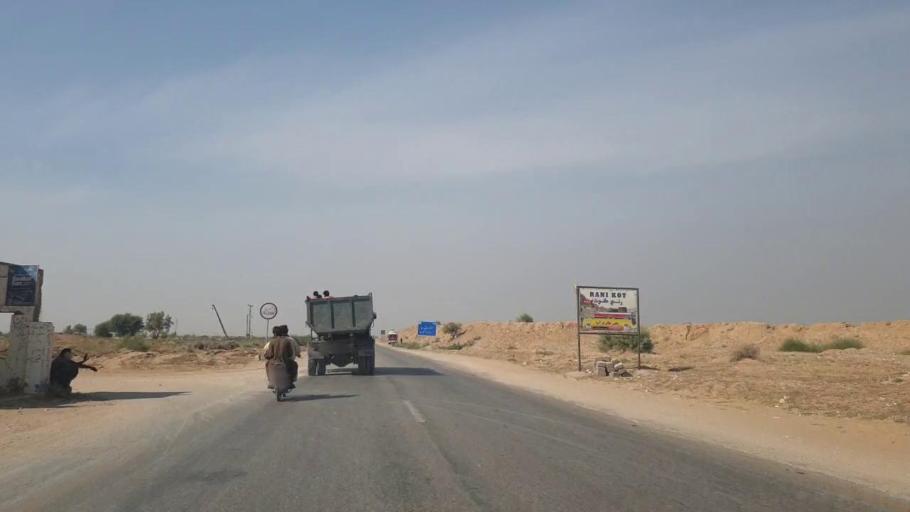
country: PK
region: Sindh
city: Sann
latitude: 26.0308
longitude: 68.1218
